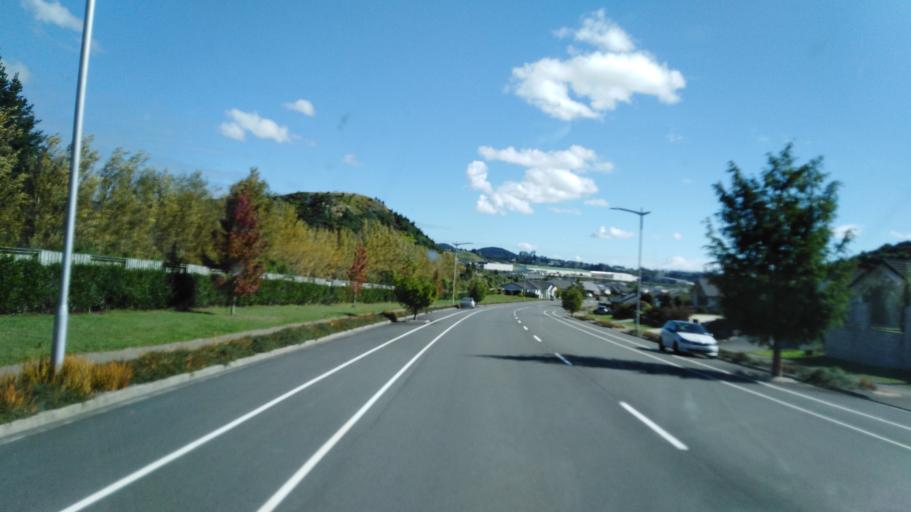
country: NZ
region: Bay of Plenty
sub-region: Tauranga City
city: Tauranga
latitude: -37.7612
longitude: 176.1045
